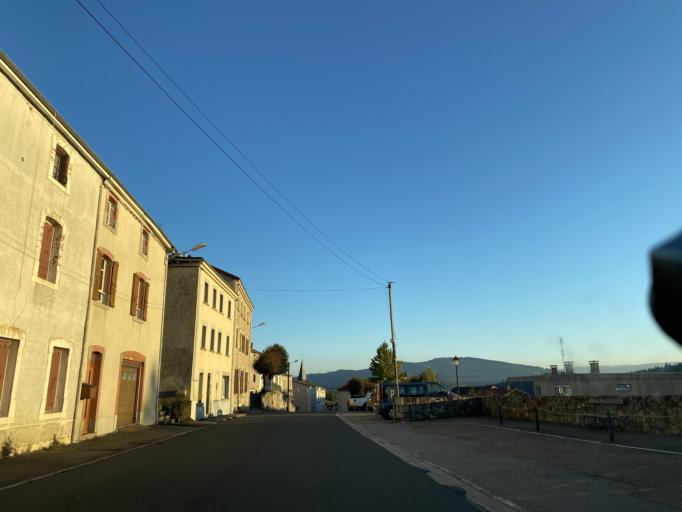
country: FR
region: Rhone-Alpes
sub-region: Departement de la Loire
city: Saint-Just-en-Chevalet
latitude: 45.9166
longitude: 3.8446
